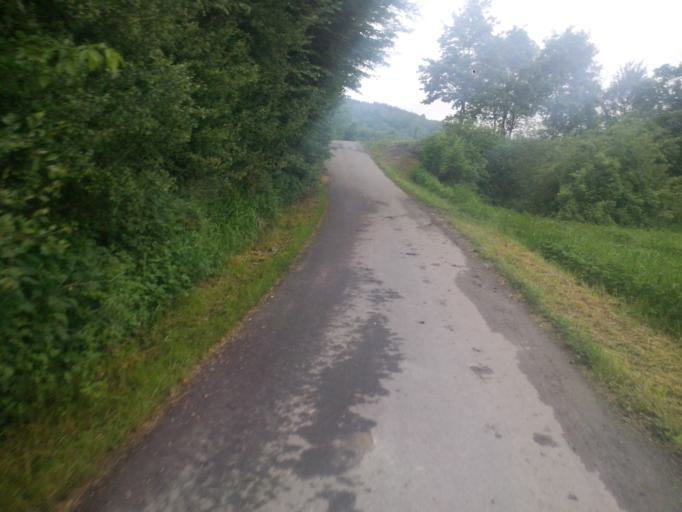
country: PL
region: Subcarpathian Voivodeship
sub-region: Powiat strzyzowski
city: Strzyzow
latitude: 49.8710
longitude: 21.8145
